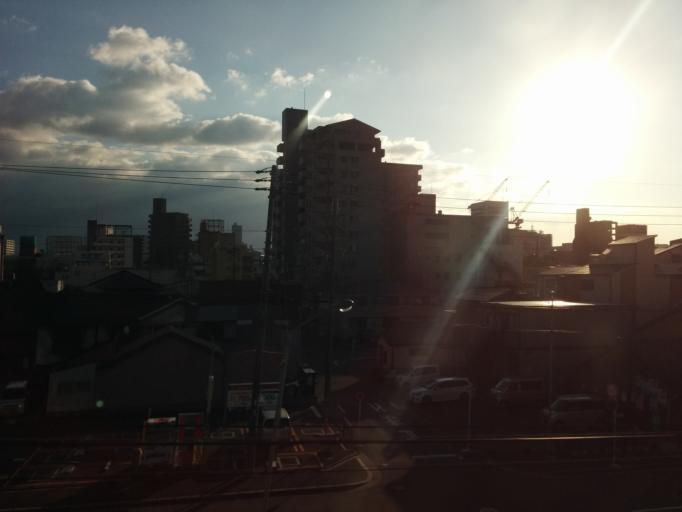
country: JP
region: Aichi
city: Nagoya-shi
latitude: 35.1463
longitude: 136.8878
